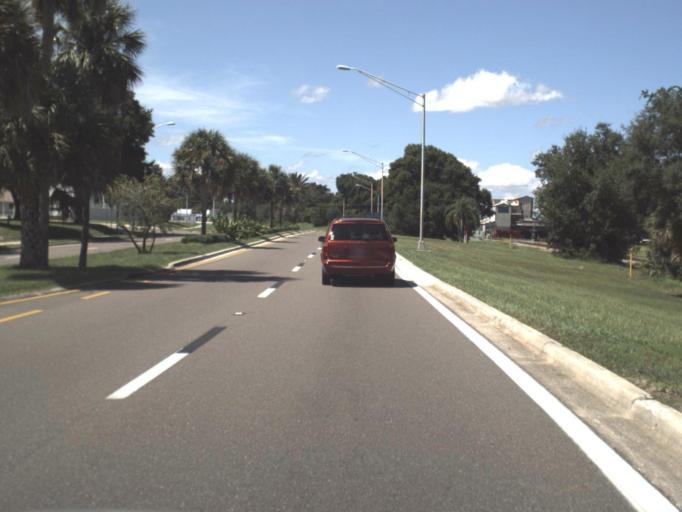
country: US
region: Florida
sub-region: Polk County
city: Lake Alfred
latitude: 28.0953
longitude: -81.7273
